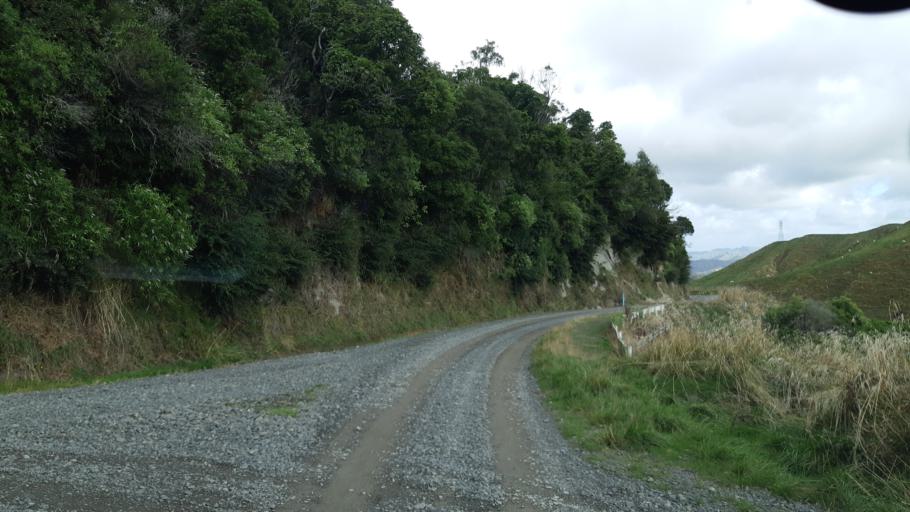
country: NZ
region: Manawatu-Wanganui
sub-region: Ruapehu District
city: Waiouru
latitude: -39.7869
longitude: 175.6803
